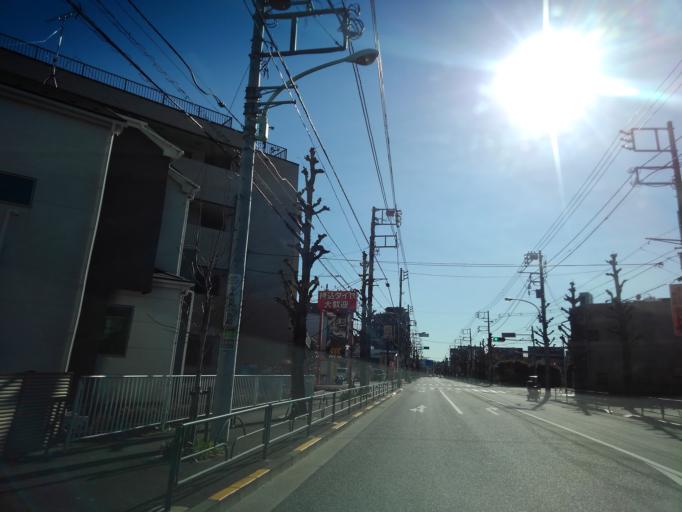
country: JP
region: Tokyo
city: Kokubunji
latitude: 35.6780
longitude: 139.4990
